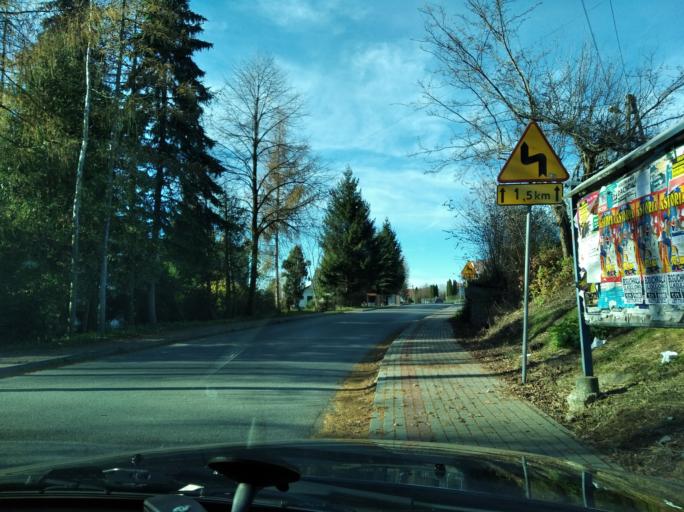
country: PL
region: Subcarpathian Voivodeship
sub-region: Powiat rzeszowski
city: Lutoryz
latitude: 49.9644
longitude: 21.9214
